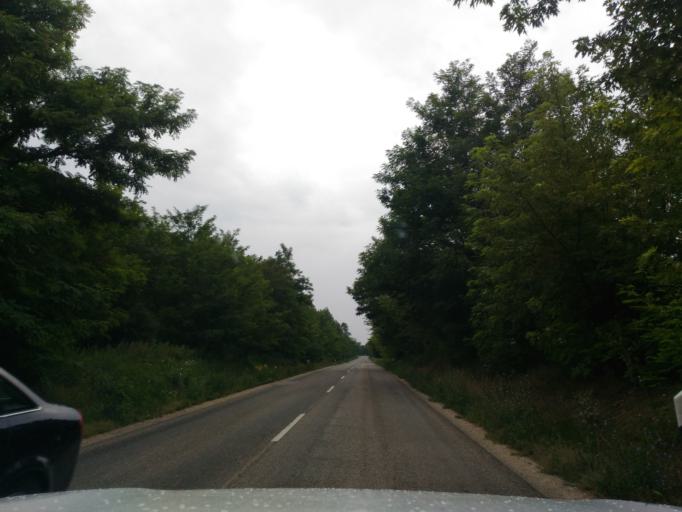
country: HU
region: Pest
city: Ujhartyan
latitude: 47.2062
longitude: 19.3645
